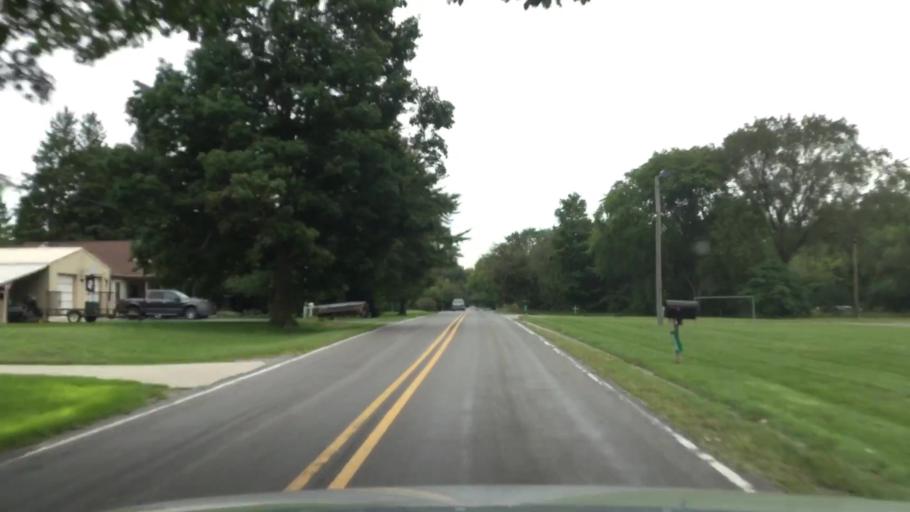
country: US
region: Michigan
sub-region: Washtenaw County
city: Milan
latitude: 42.1617
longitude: -83.6504
